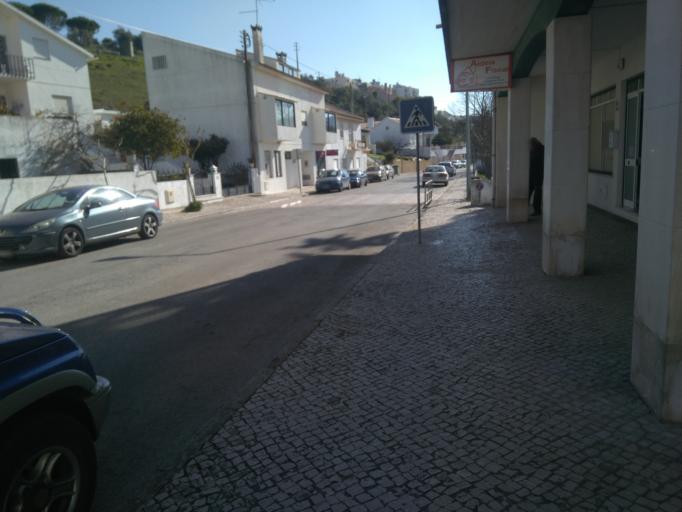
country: PT
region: Leiria
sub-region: Porto de Mos
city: Porto de Mos
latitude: 39.6010
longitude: -8.8157
